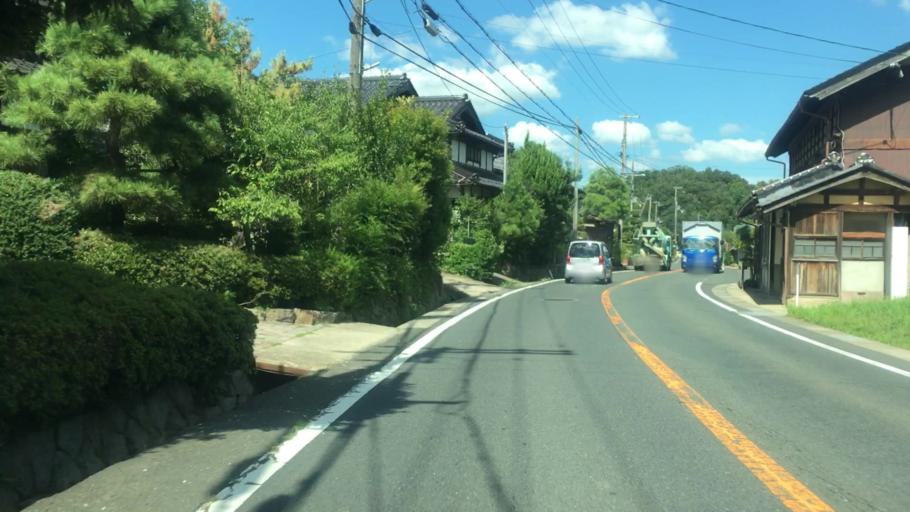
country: JP
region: Kyoto
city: Miyazu
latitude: 35.5923
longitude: 135.0408
